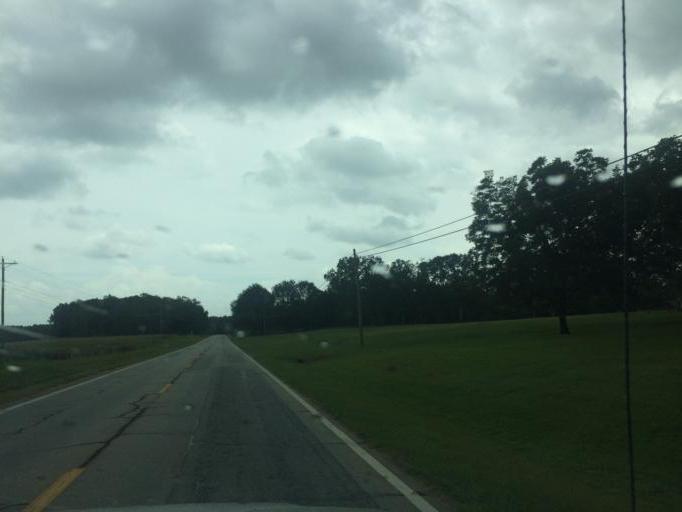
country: US
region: Georgia
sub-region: Elbert County
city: Elberton
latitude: 34.1716
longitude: -82.8799
